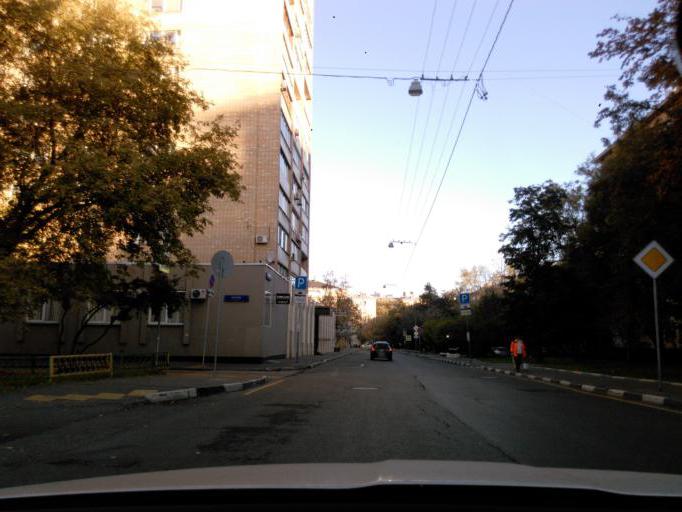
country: RU
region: Moskovskaya
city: Dorogomilovo
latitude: 55.7684
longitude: 37.5868
